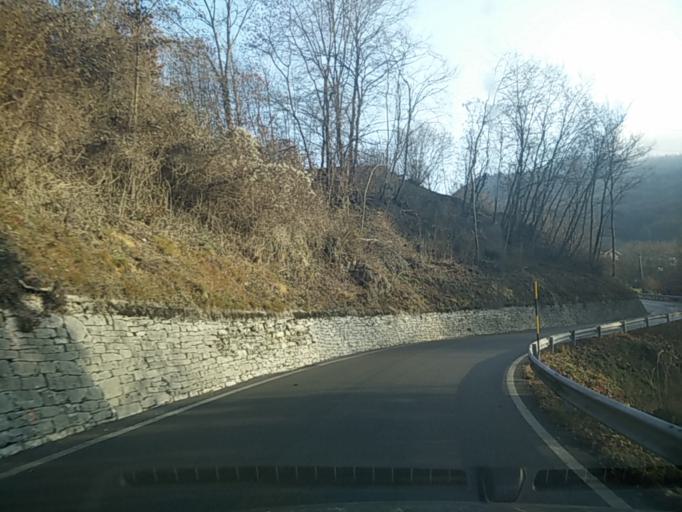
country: IT
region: Veneto
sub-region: Provincia di Belluno
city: Trichiana
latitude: 46.0344
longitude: 12.1625
